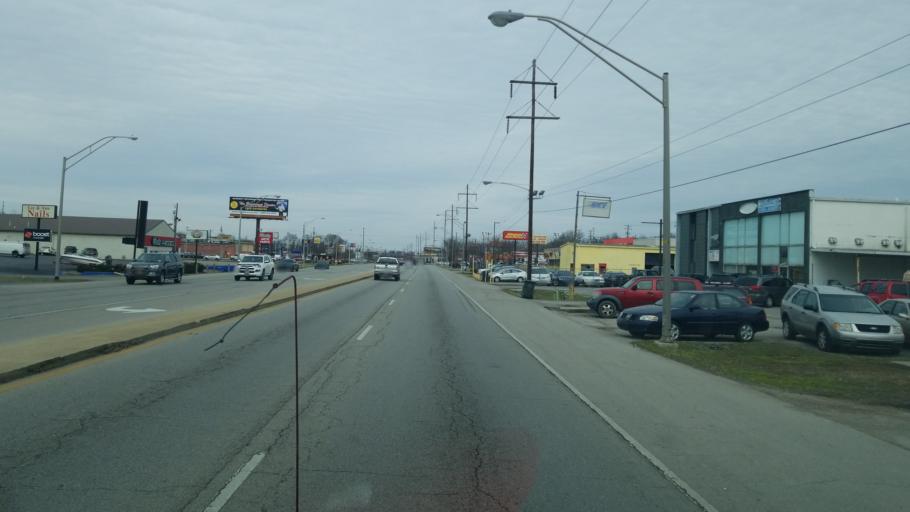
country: US
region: Kentucky
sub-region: Fayette County
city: Lexington-Fayette
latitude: 38.0629
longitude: -84.4676
